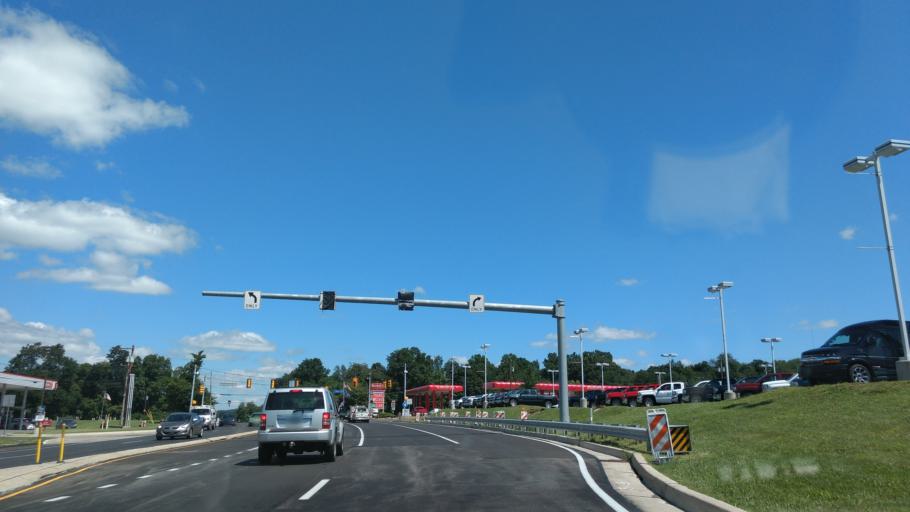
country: US
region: Pennsylvania
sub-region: Beaver County
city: Baden
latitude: 40.6253
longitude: -80.2292
